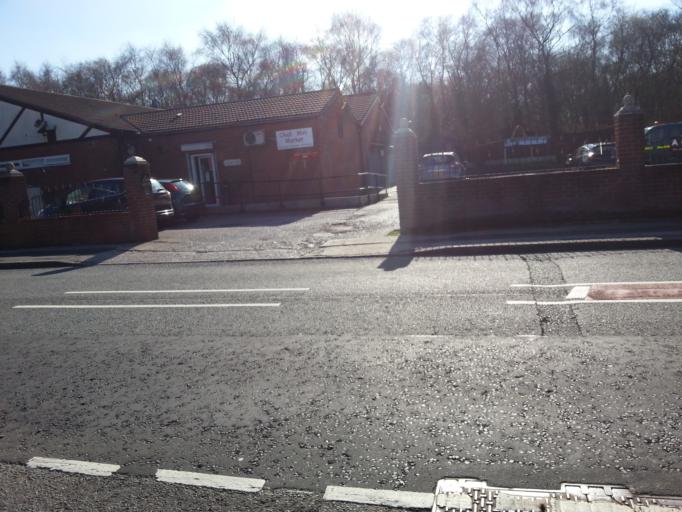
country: GB
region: England
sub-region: Knowsley
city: Huyton
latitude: 53.3690
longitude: -2.8417
